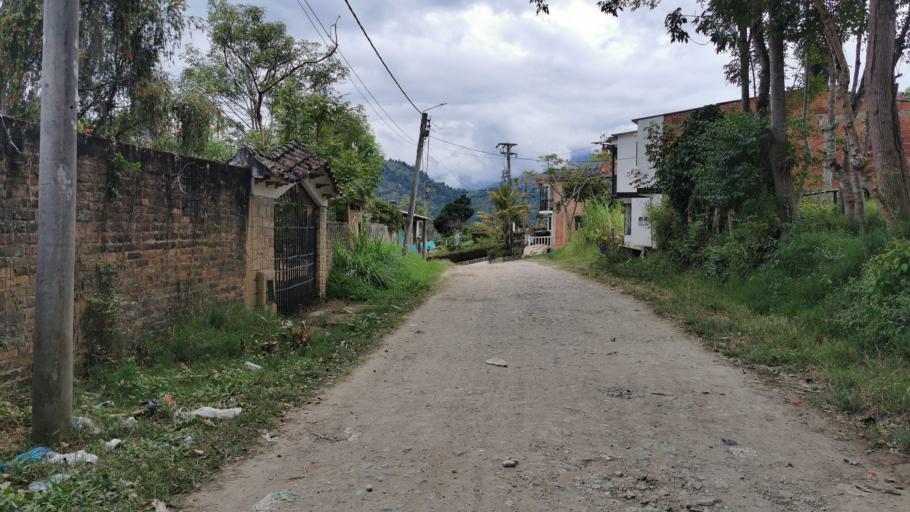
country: CO
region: Cundinamarca
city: Tenza
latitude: 5.0759
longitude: -73.4234
